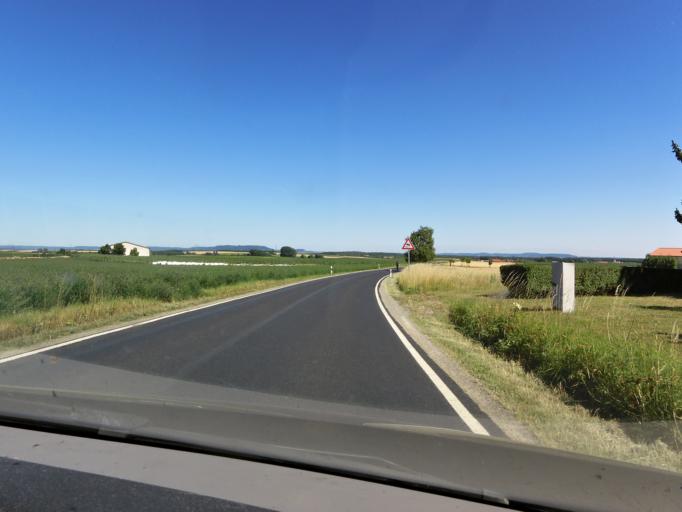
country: DE
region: Bavaria
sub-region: Regierungsbezirk Unterfranken
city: Biebelried
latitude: 49.7440
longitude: 10.0685
